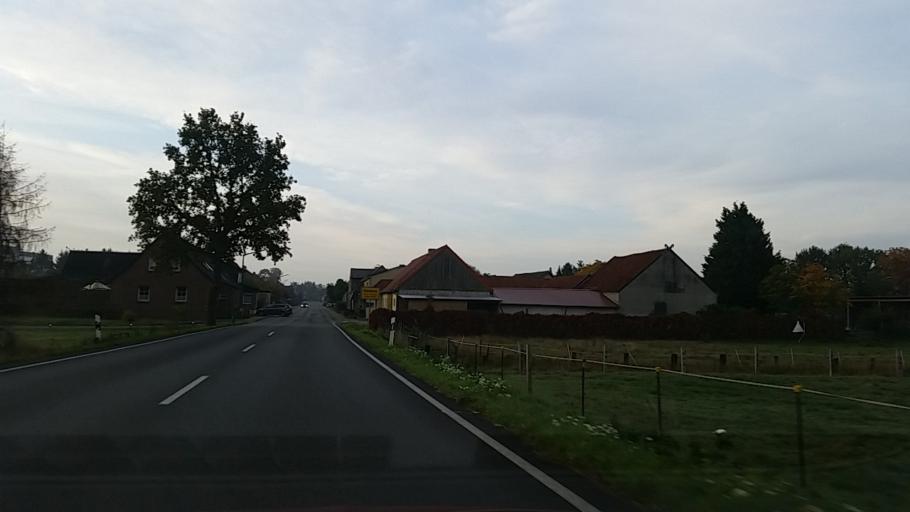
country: DE
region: Saxony-Anhalt
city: Jubar
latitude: 52.6517
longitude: 10.8613
